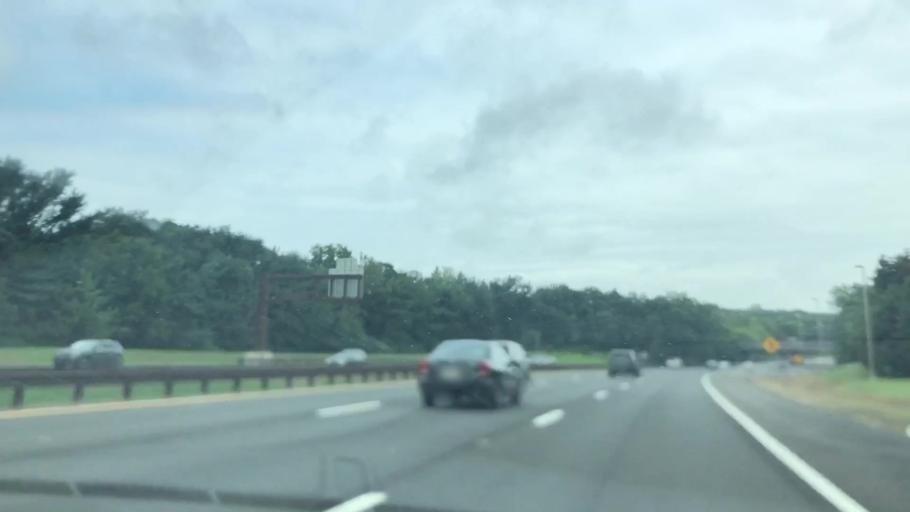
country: US
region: New Jersey
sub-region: Bergen County
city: Paramus
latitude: 40.9741
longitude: -74.0689
